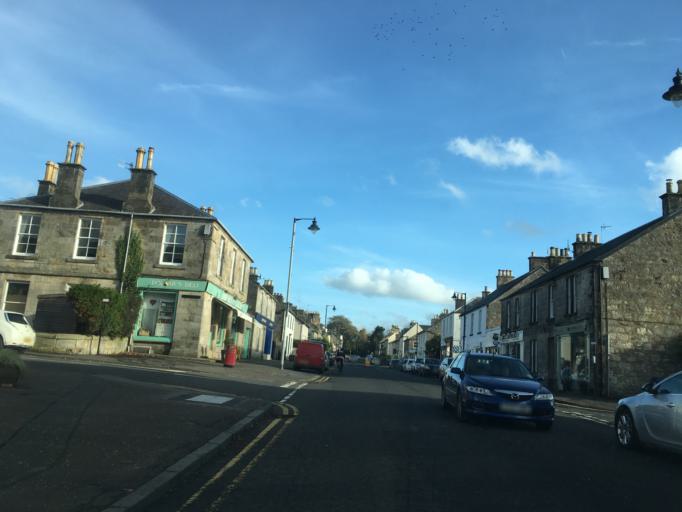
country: GB
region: Scotland
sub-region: Clackmannanshire
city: Dollar
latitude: 56.1627
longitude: -3.6752
